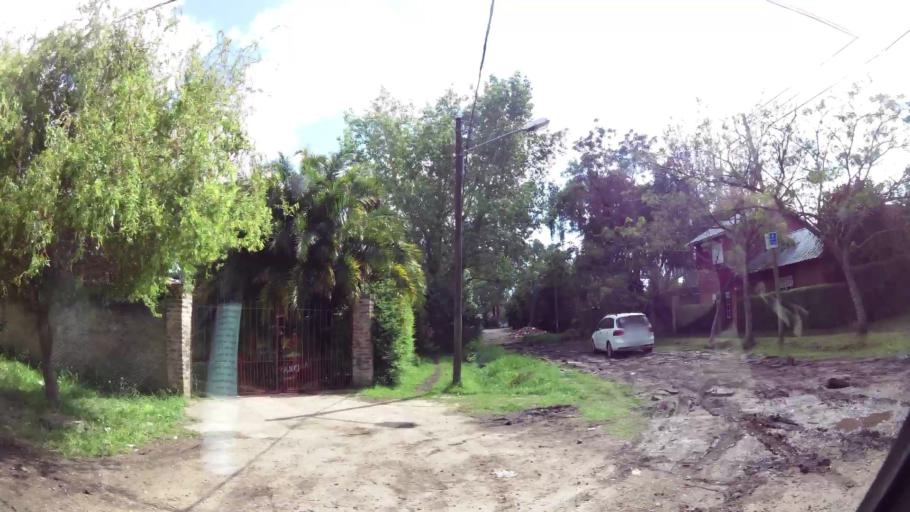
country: AR
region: Buenos Aires
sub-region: Partido de Quilmes
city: Quilmes
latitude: -34.8280
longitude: -58.1853
